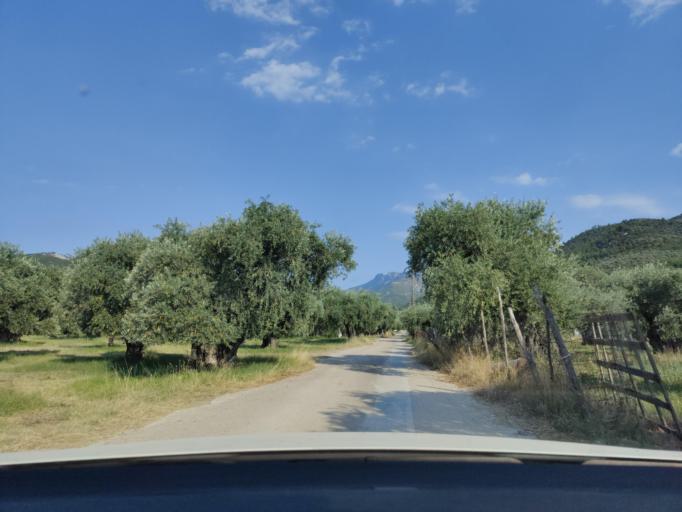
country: GR
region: East Macedonia and Thrace
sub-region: Nomos Kavalas
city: Prinos
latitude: 40.7695
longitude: 24.5967
